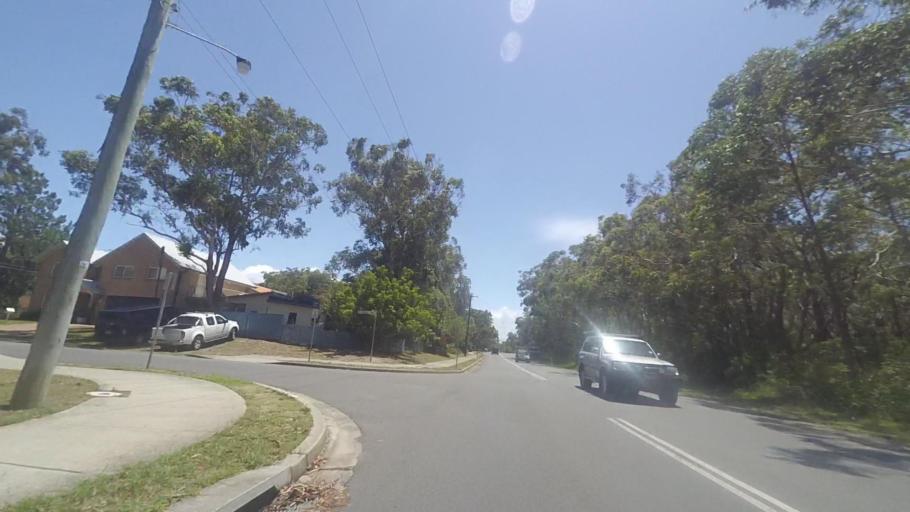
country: AU
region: New South Wales
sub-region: Great Lakes
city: Hawks Nest
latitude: -32.6698
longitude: 152.1779
